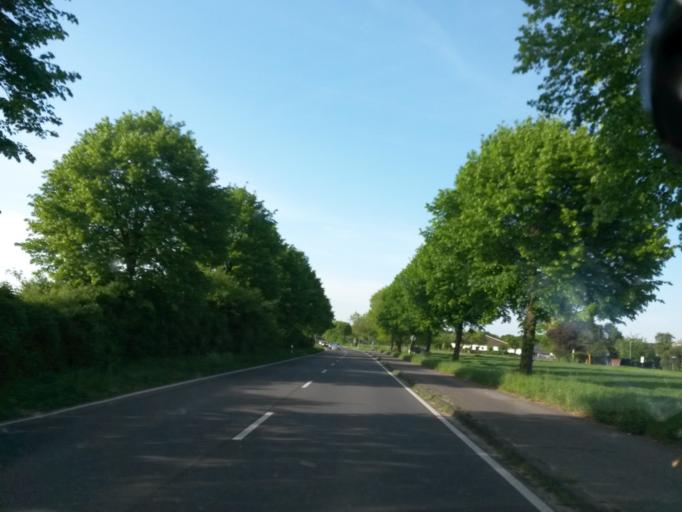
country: DE
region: North Rhine-Westphalia
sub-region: Regierungsbezirk Koln
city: Hennef
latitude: 50.8378
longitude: 7.2875
